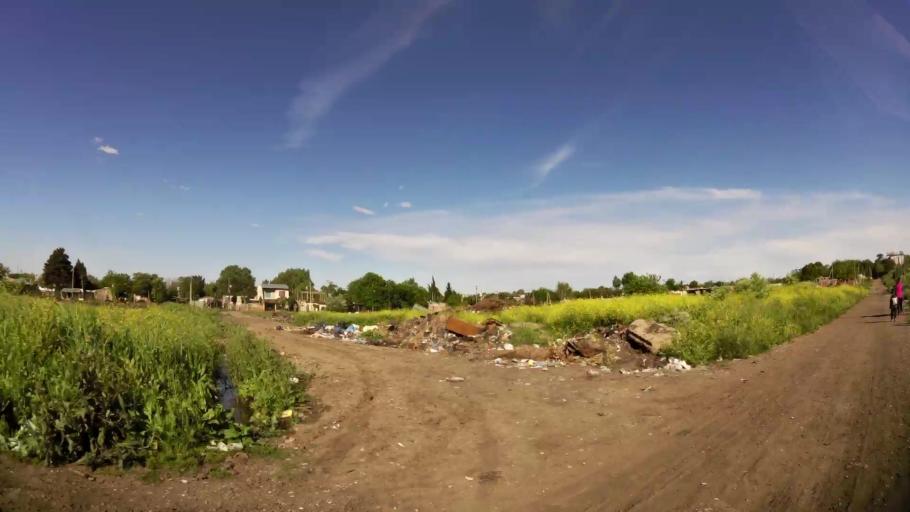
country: AR
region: Buenos Aires
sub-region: Partido de Almirante Brown
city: Adrogue
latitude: -34.8256
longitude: -58.3560
